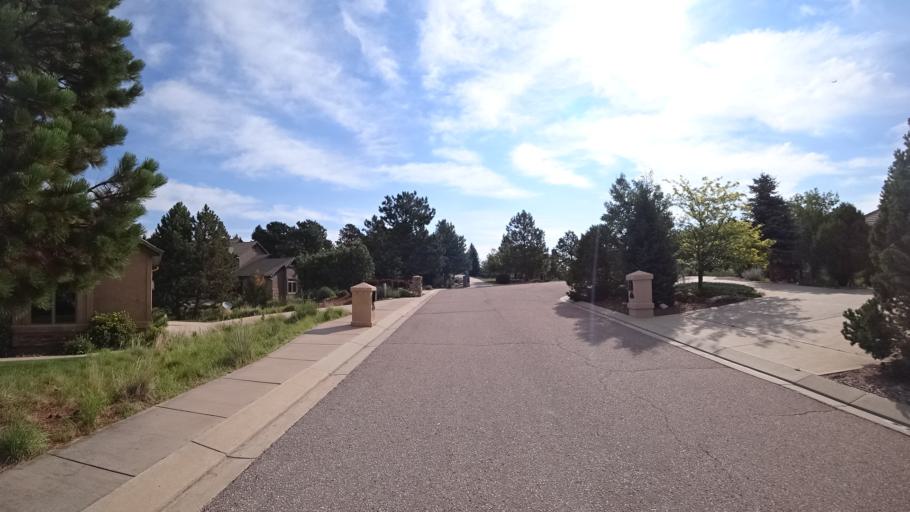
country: US
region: Colorado
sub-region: El Paso County
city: Air Force Academy
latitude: 38.9424
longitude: -104.8294
